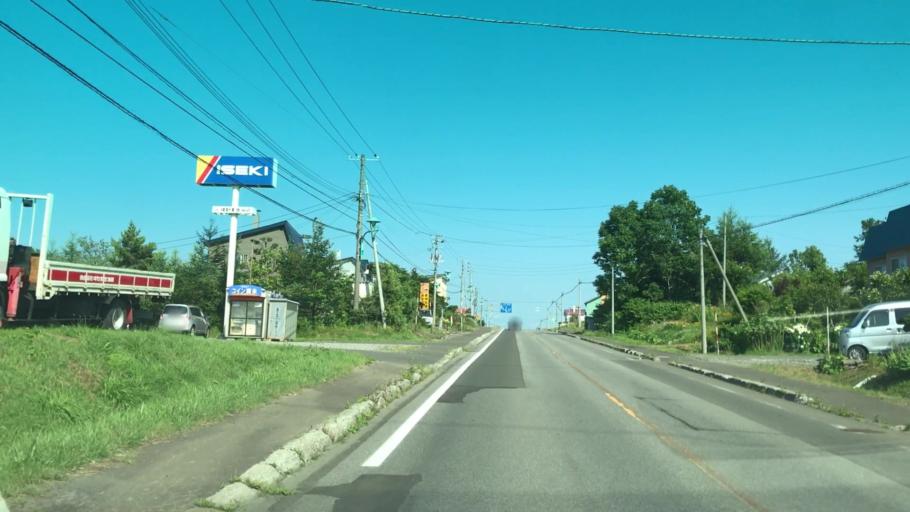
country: JP
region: Hokkaido
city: Iwanai
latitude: 42.9822
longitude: 140.5697
